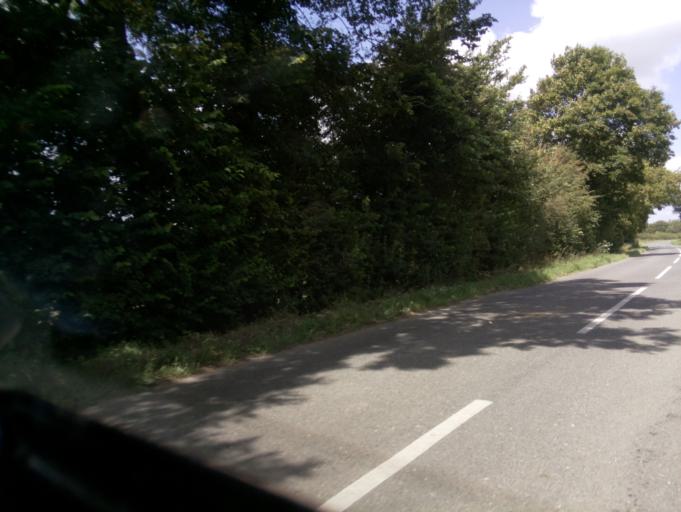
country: GB
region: England
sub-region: Oxfordshire
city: Faringdon
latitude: 51.6418
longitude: -1.5911
